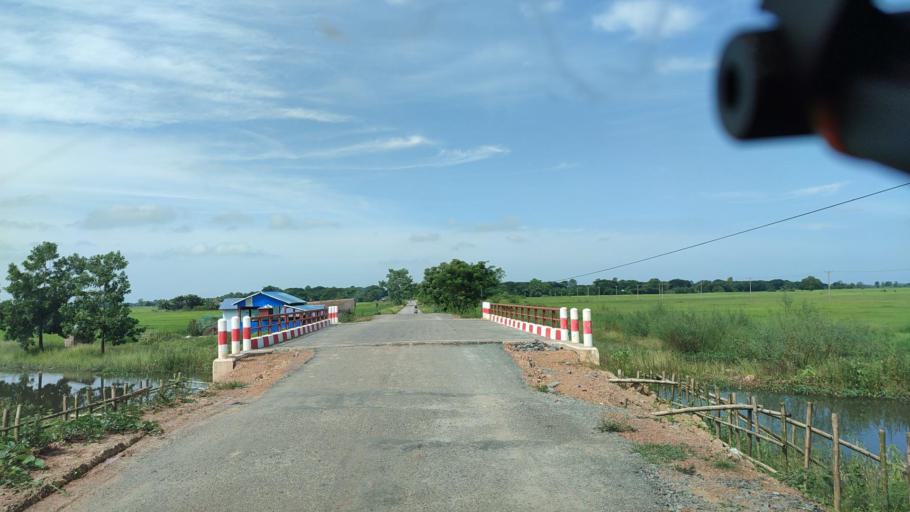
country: MM
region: Ayeyarwady
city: Hinthada
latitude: 17.7154
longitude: 95.5939
